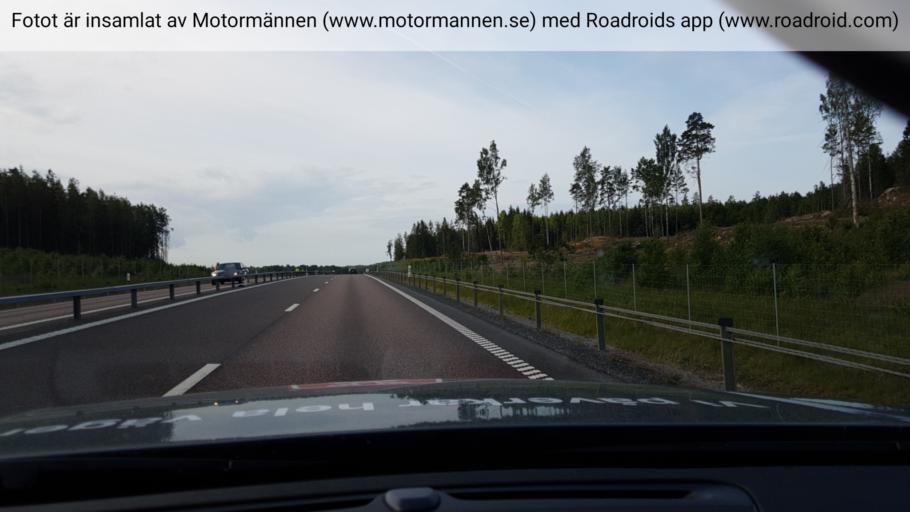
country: SE
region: OErebro
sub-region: Askersunds Kommun
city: Askersund
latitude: 58.8408
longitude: 14.9064
